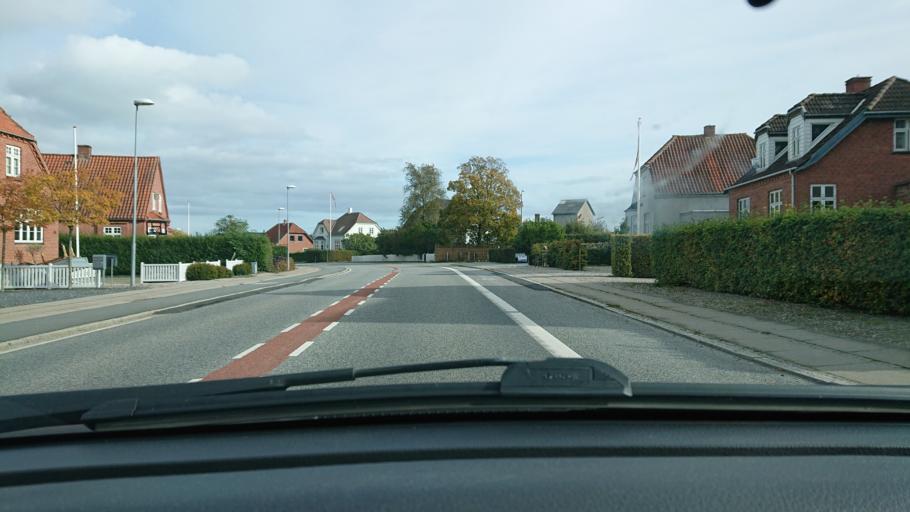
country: DK
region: South Denmark
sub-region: Nyborg Kommune
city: Nyborg
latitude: 55.3088
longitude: 10.7647
